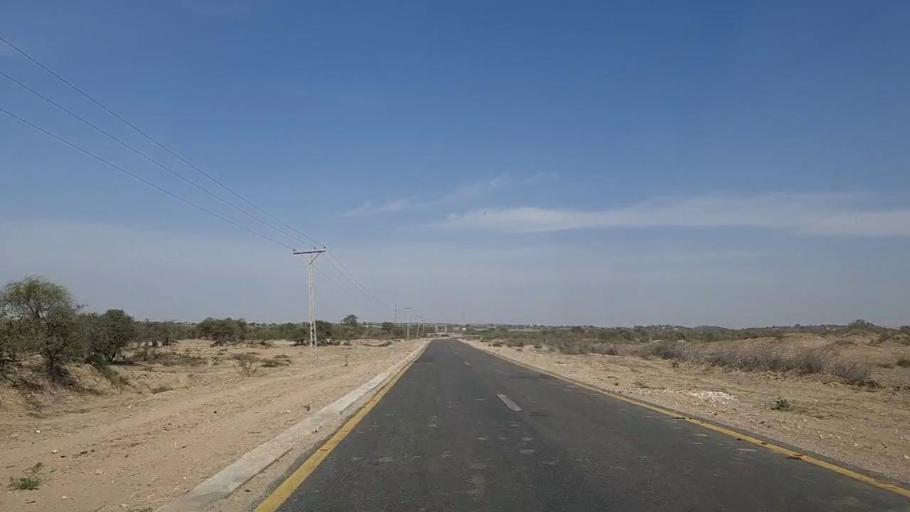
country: PK
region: Sindh
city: Mithi
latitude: 24.9628
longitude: 69.9098
